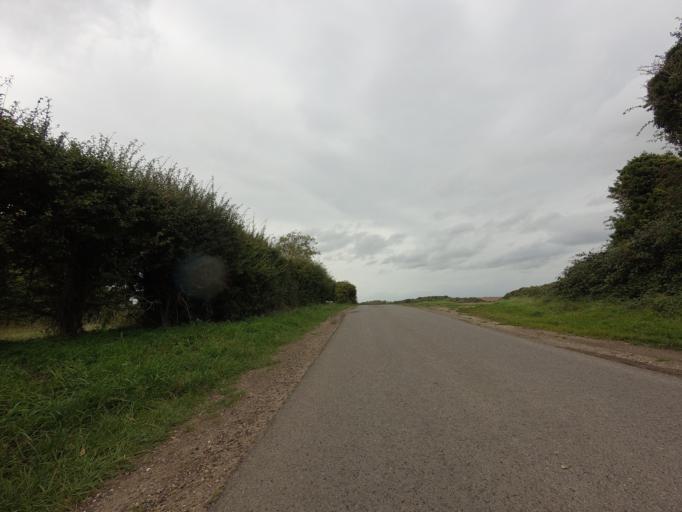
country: GB
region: England
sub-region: Cambridgeshire
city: Duxford
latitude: 52.0499
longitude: 0.1369
